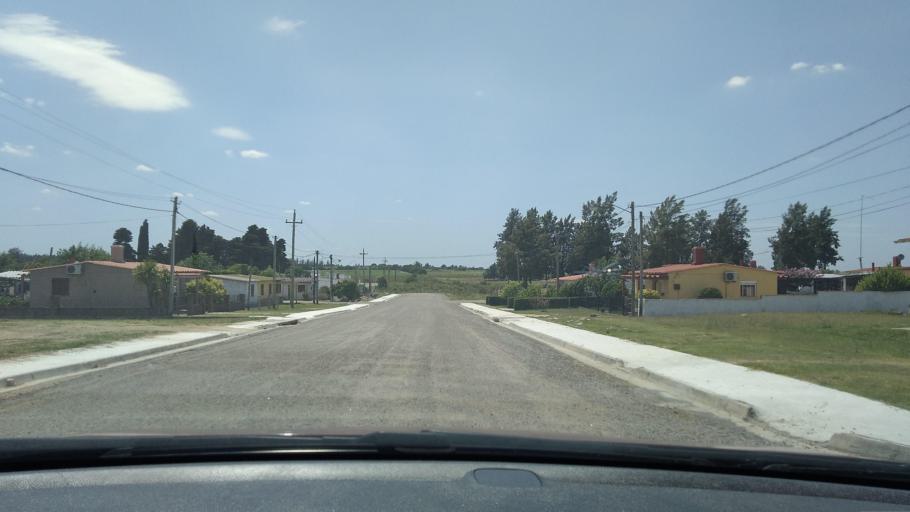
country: UY
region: Canelones
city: Tala
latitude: -34.2055
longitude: -55.7428
